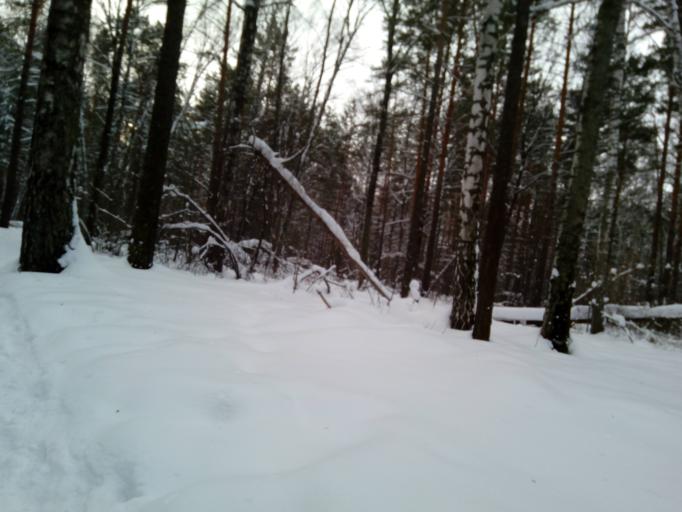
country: RU
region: Novosibirsk
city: Akademgorodok
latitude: 54.8589
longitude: 83.0929
